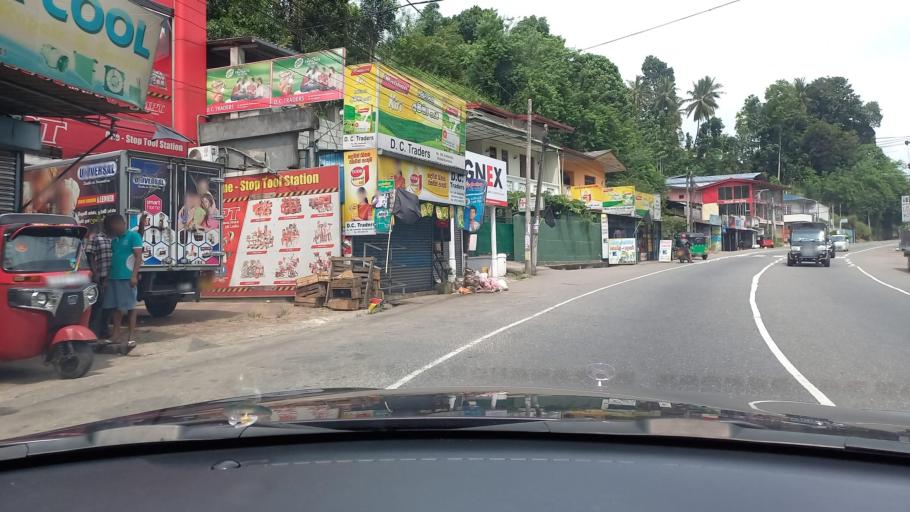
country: LK
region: Central
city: Kadugannawa
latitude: 7.2686
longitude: 80.5805
